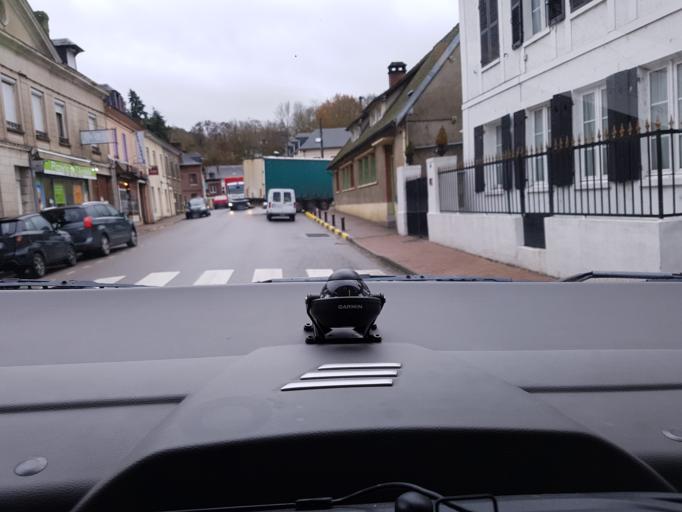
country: FR
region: Haute-Normandie
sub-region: Departement de l'Eure
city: Pont-Saint-Pierre
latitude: 49.3317
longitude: 1.2796
